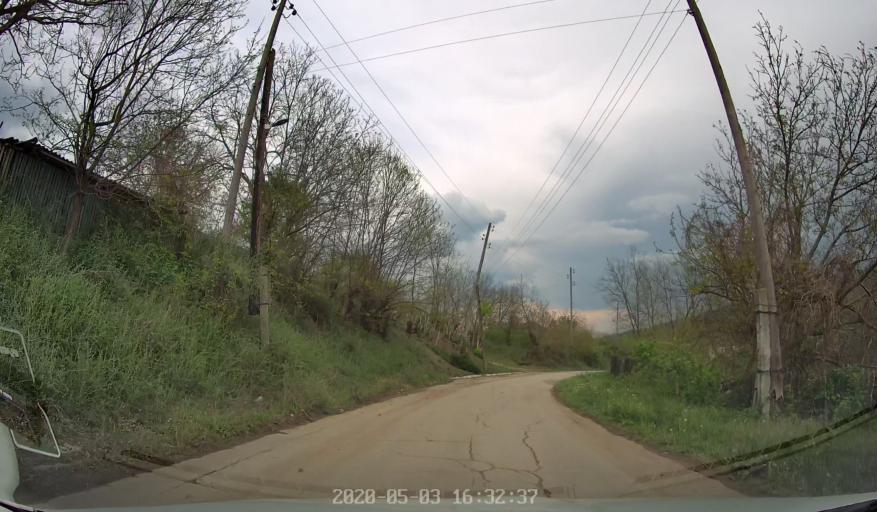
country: MD
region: Calarasi
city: Calarasi
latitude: 47.1921
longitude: 28.3367
